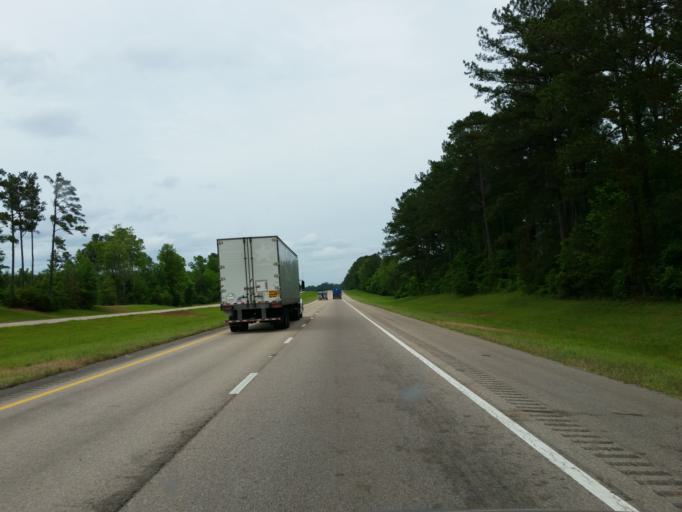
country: US
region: Mississippi
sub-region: Clarke County
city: Stonewall
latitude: 32.0033
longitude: -88.9349
